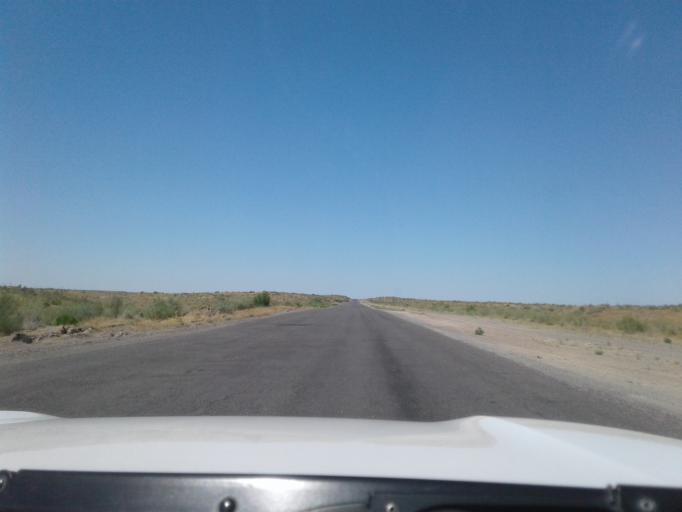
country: TM
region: Mary
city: Bayramaly
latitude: 38.0196
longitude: 62.7374
